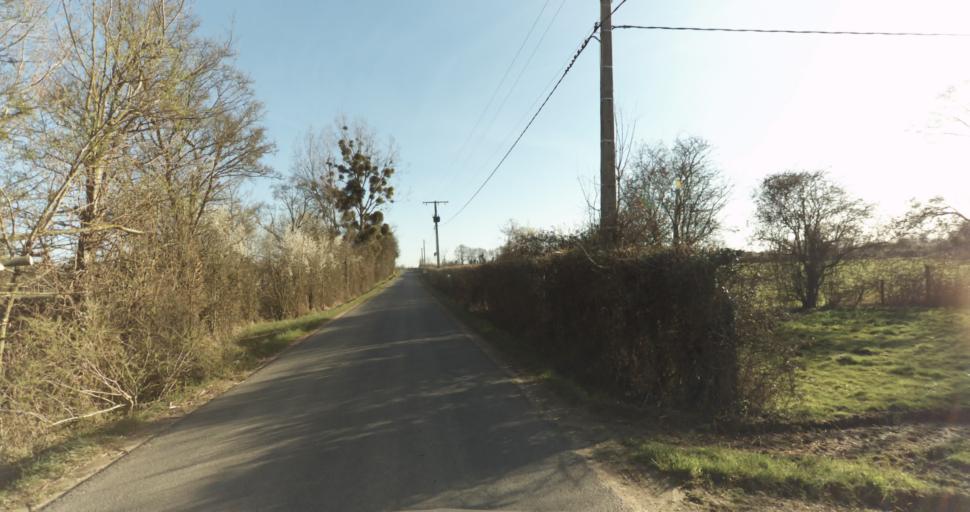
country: FR
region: Lower Normandy
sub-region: Departement de l'Orne
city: Trun
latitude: 48.9311
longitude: 0.0304
